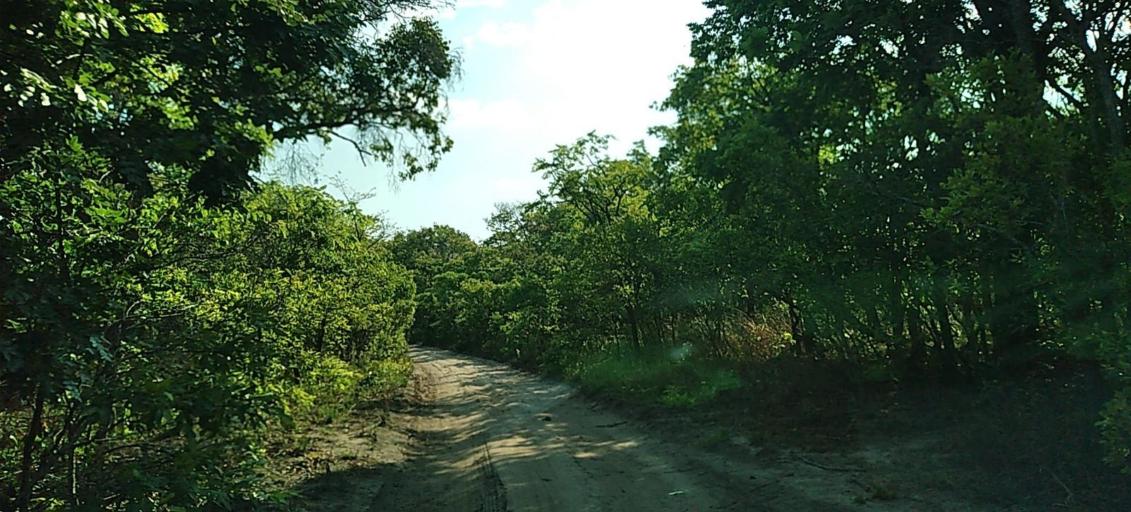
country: ZM
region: North-Western
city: Mwinilunga
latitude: -11.3165
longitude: 24.7411
